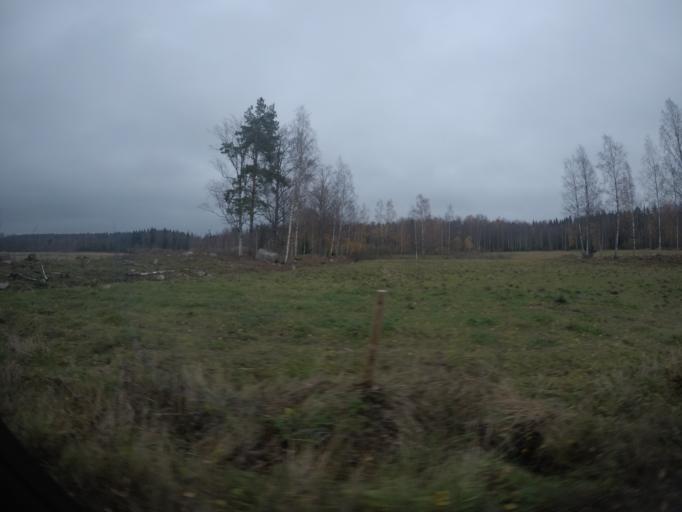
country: SE
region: Vaestmanland
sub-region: Surahammars Kommun
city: Surahammar
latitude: 59.6762
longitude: 16.0818
